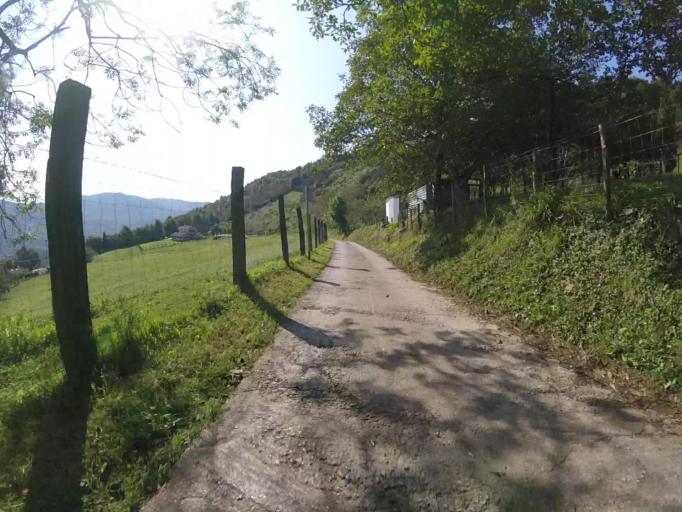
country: ES
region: Basque Country
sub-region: Provincia de Guipuzcoa
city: Irun
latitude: 43.3282
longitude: -1.7589
